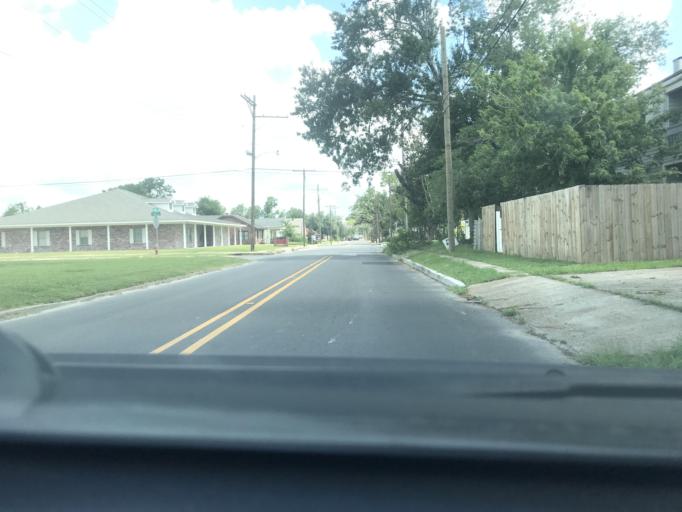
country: US
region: Louisiana
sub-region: Calcasieu Parish
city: Lake Charles
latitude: 30.2136
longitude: -93.2160
